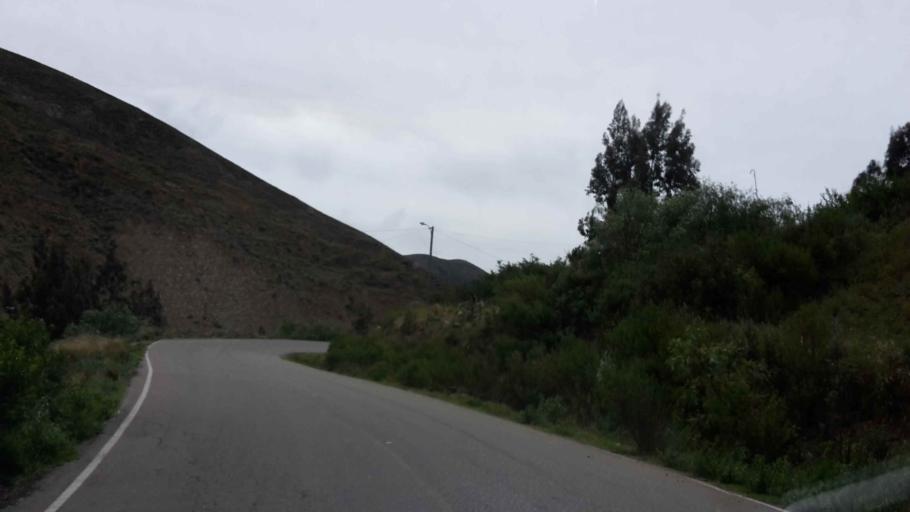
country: BO
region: Cochabamba
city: Colomi
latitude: -17.4019
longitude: -65.7940
